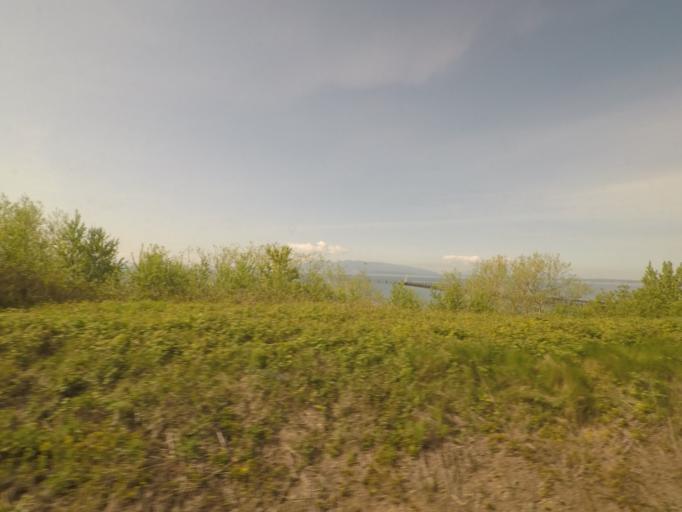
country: US
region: Washington
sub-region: Whatcom County
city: Bellingham
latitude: 48.7640
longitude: -122.5154
